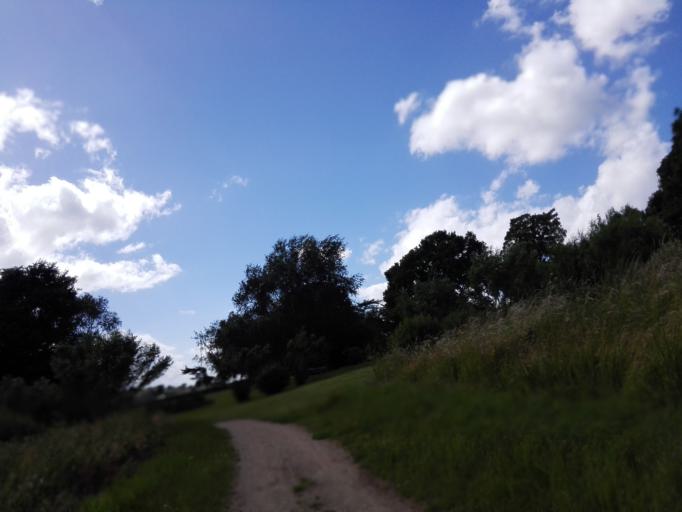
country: DK
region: Capital Region
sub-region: Allerod Kommune
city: Lynge
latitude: 55.8189
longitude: 12.2752
